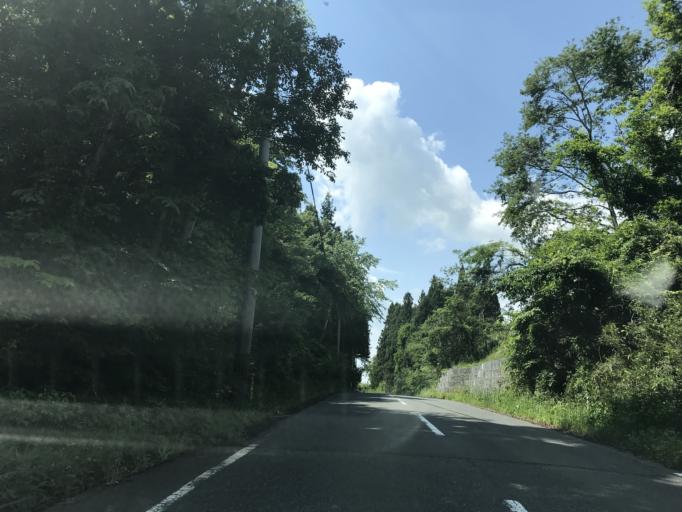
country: JP
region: Miyagi
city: Furukawa
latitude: 38.7072
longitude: 140.9336
